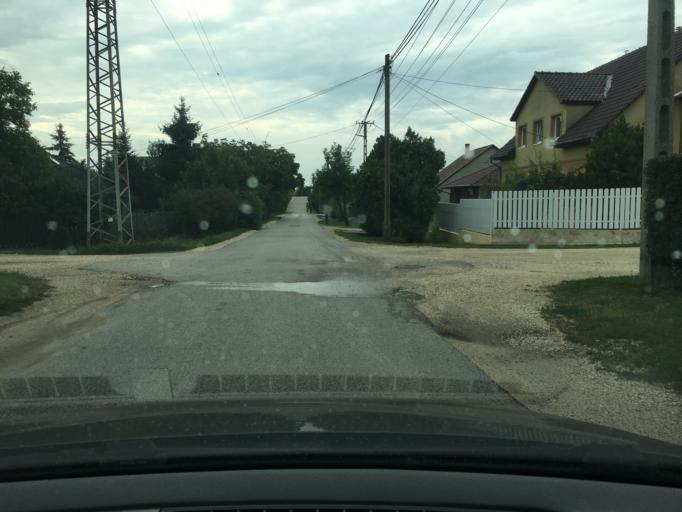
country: HU
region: Pest
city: Erd
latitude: 47.3920
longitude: 18.9031
